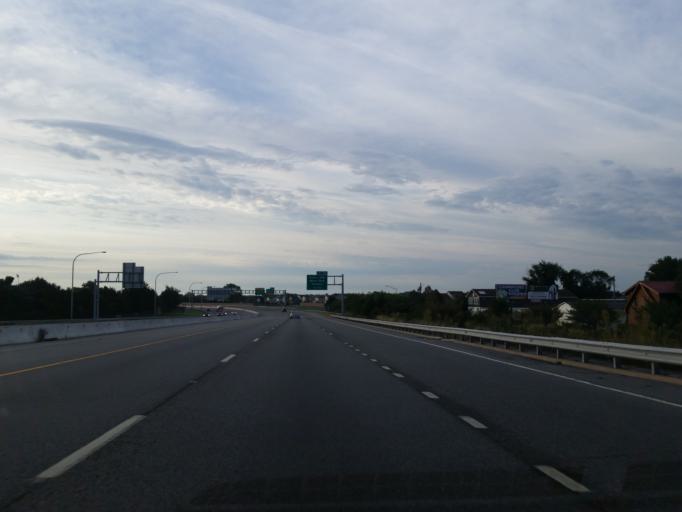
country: US
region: Delaware
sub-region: Kent County
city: Dover Base Housing
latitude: 39.1288
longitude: -75.4909
